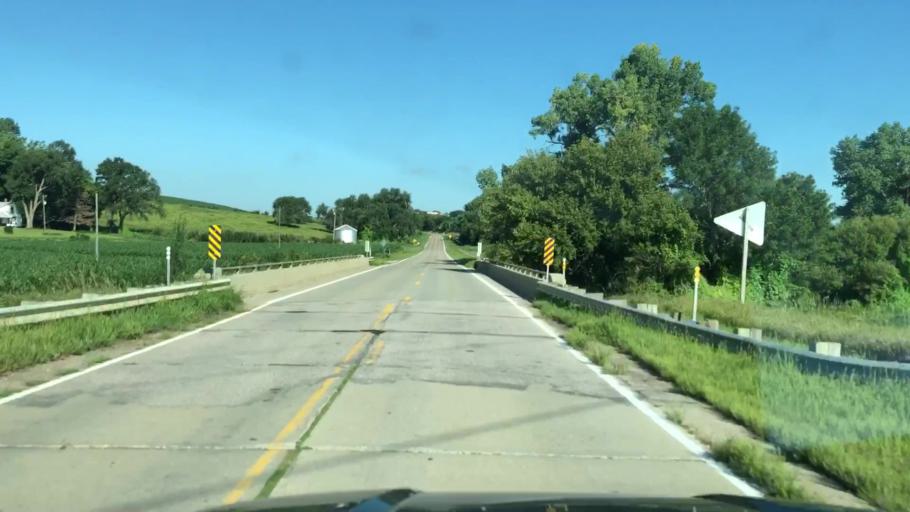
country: US
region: Iowa
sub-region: Woodbury County
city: Sergeant Bluff
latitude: 42.4167
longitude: -96.2630
